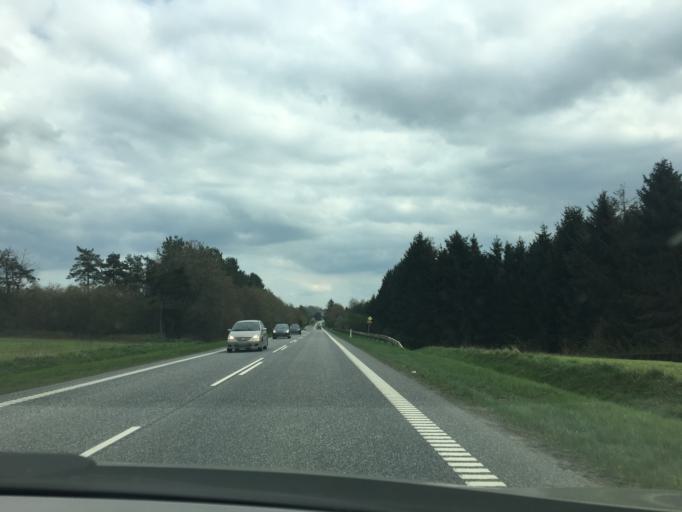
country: DK
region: Central Jutland
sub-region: Horsens Kommune
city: Braedstrup
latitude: 55.9424
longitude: 9.6486
